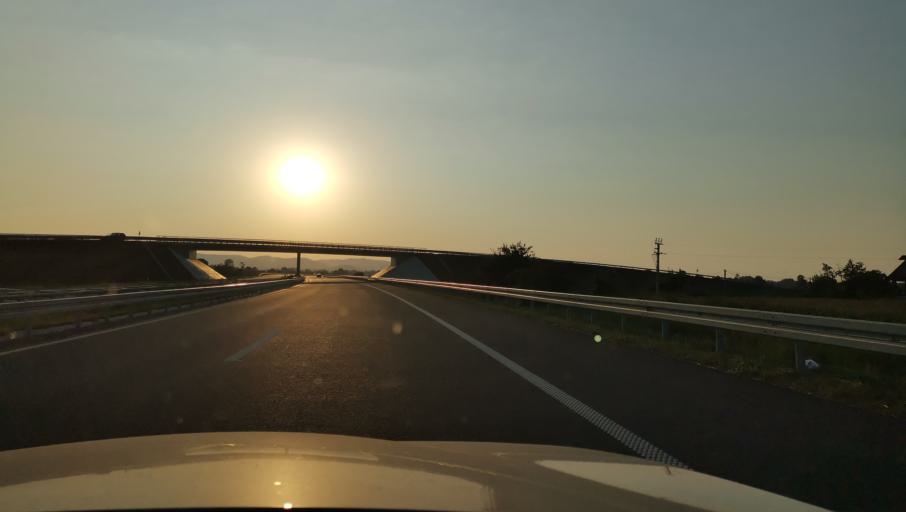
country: RS
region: Central Serbia
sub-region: Kolubarski Okrug
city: Lajkovac
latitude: 44.3467
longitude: 20.1777
